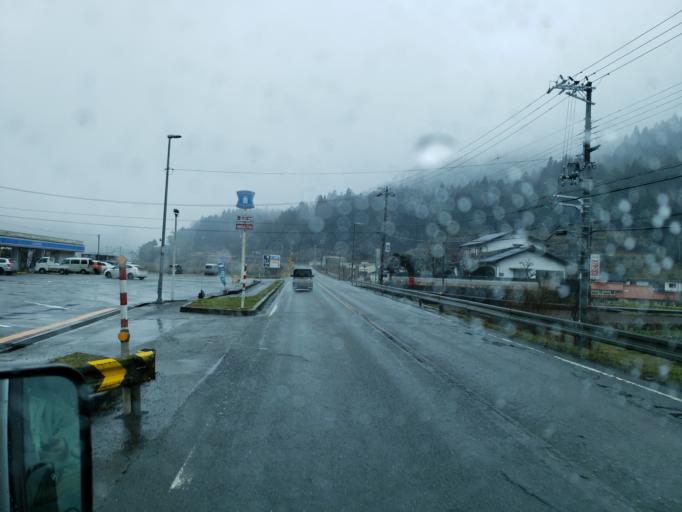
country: JP
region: Hyogo
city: Toyooka
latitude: 35.3832
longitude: 134.6742
